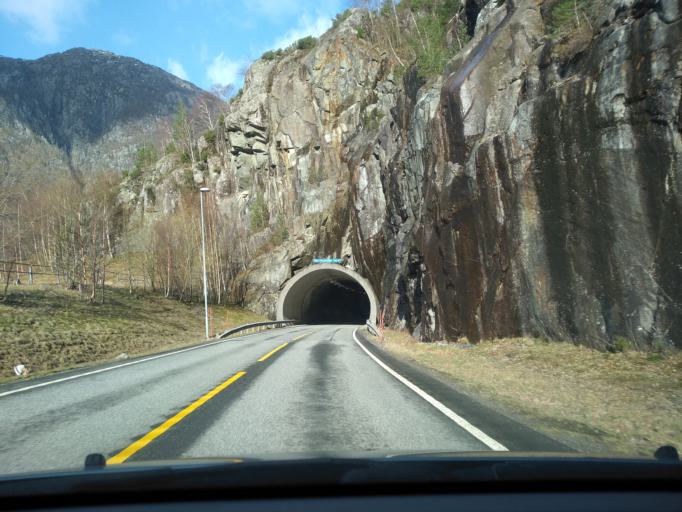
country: NO
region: Rogaland
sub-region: Sauda
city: Sauda
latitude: 59.8598
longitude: 6.3582
